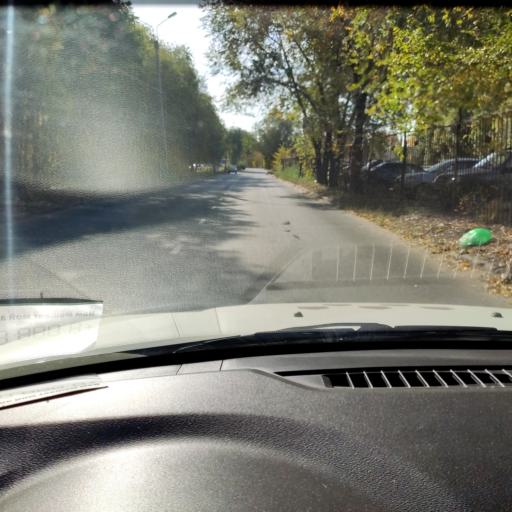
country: RU
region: Samara
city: Tol'yatti
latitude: 53.5533
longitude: 49.3088
